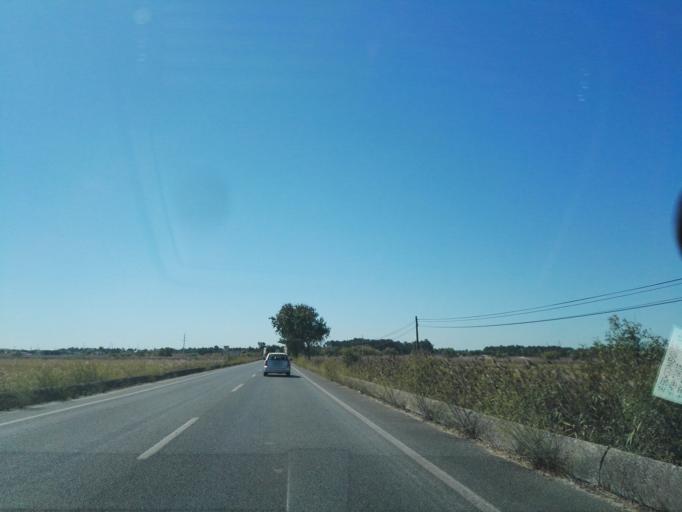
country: PT
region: Santarem
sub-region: Benavente
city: Samora Correia
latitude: 38.9399
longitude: -8.8417
